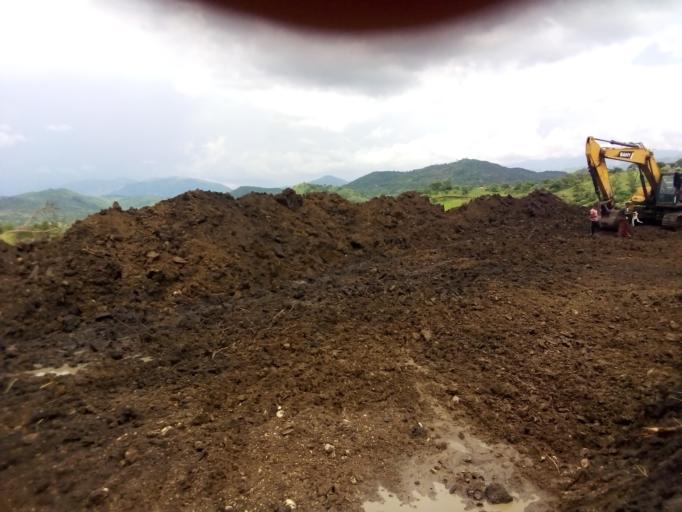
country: ET
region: Oromiya
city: Jima
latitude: 7.2163
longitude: 37.1332
